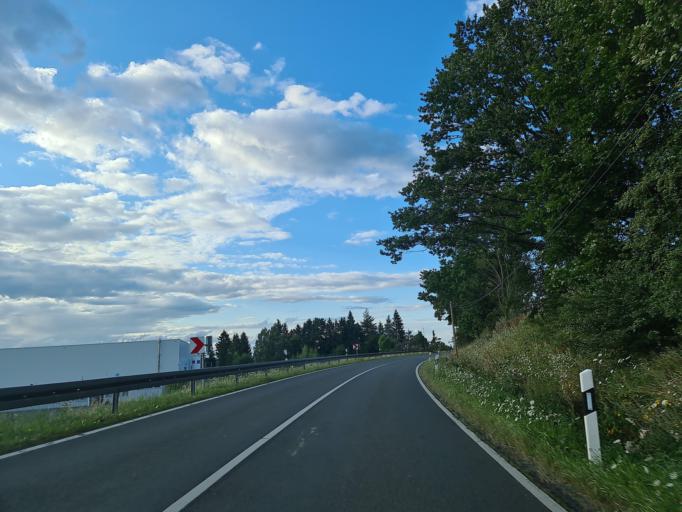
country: DE
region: Saxony
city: Pausa
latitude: 50.5900
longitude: 11.9975
